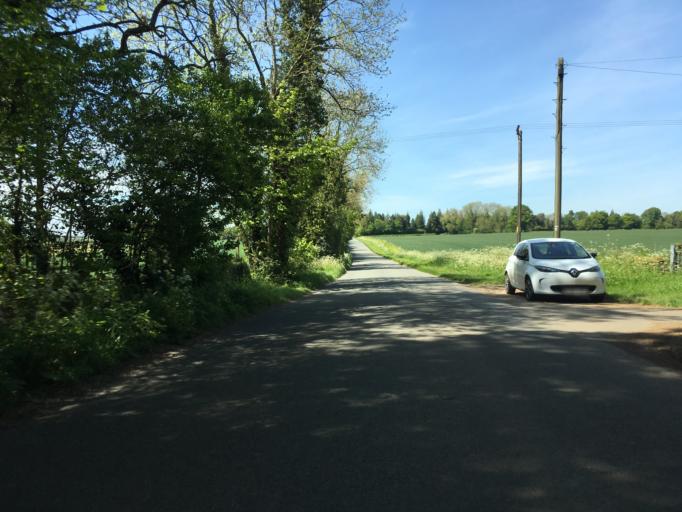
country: GB
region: England
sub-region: Gloucestershire
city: Coates
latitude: 51.6996
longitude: -2.0247
